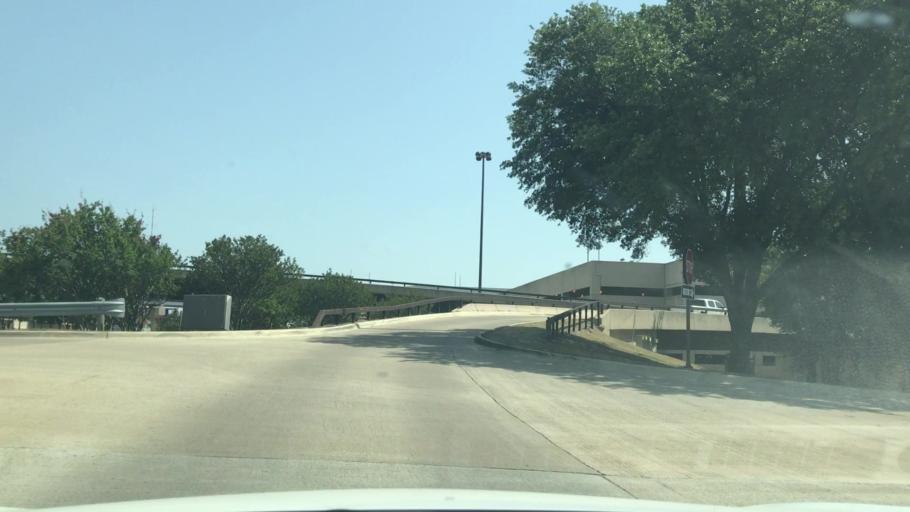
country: US
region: Texas
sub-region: Tarrant County
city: Grapevine
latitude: 32.9043
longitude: -97.0417
